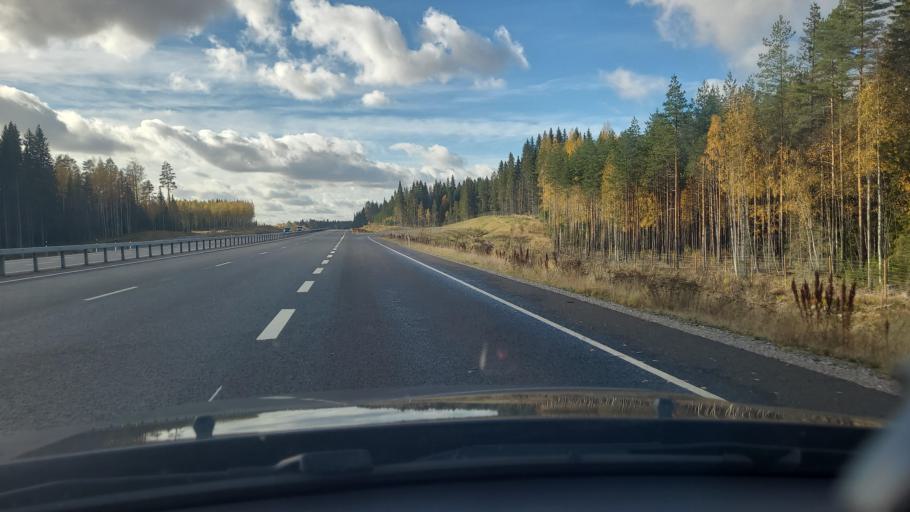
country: FI
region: Southern Savonia
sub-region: Pieksaemaeki
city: Juva
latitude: 61.8420
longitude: 27.6670
